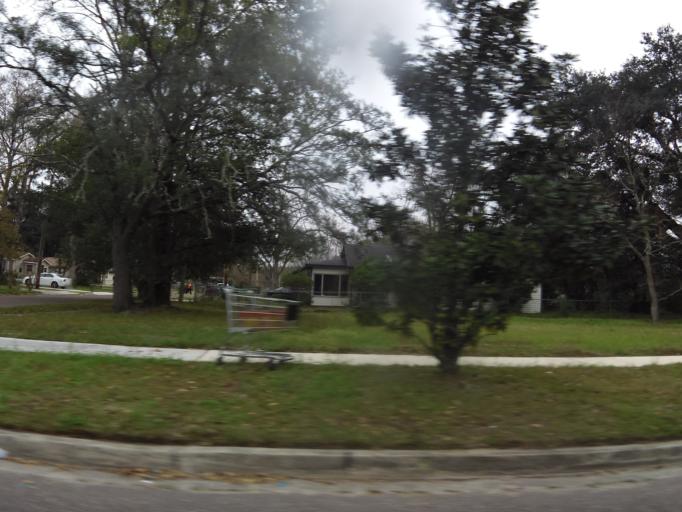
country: US
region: Florida
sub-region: Duval County
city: Jacksonville
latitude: 30.3731
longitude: -81.6935
